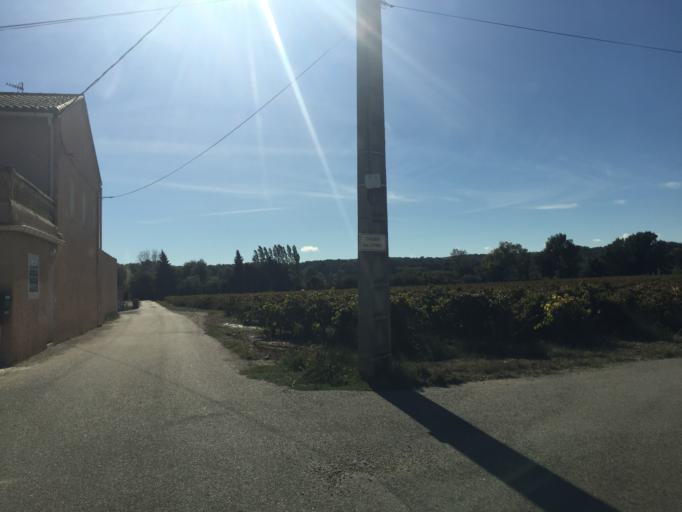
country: FR
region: Provence-Alpes-Cote d'Azur
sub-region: Departement du Vaucluse
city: Courthezon
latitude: 44.0935
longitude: 4.8626
